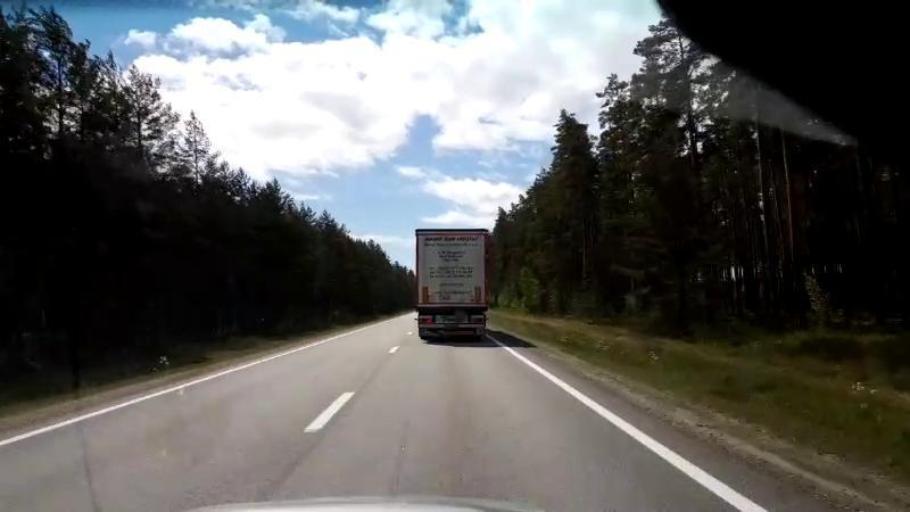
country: LV
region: Salacgrivas
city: Salacgriva
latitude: 57.5515
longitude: 24.4329
